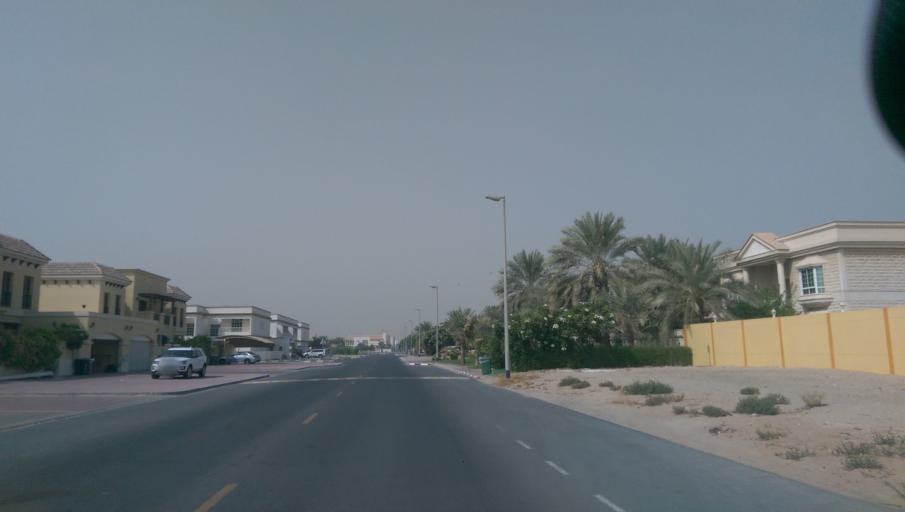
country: AE
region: Dubai
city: Dubai
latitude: 25.1534
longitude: 55.2231
